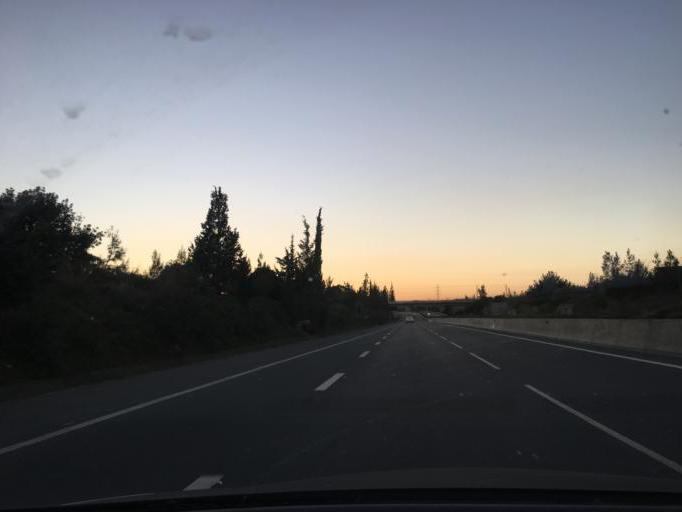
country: CY
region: Larnaka
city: Dhromolaxia
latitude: 34.9074
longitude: 33.5655
